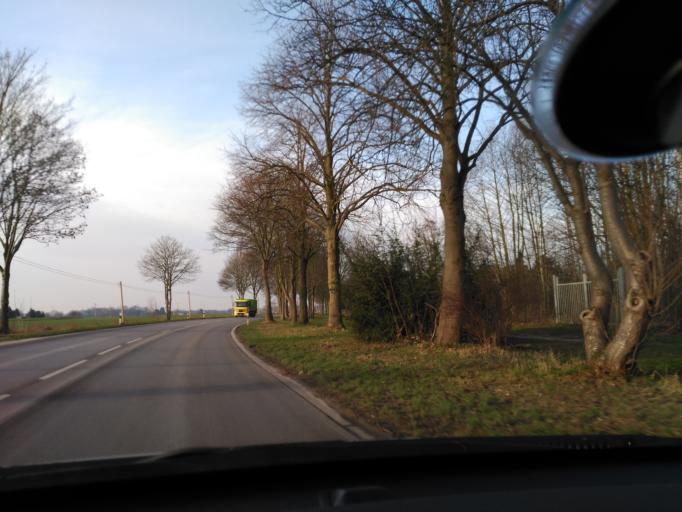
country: DE
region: North Rhine-Westphalia
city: Wegberg
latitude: 51.1444
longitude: 6.3642
